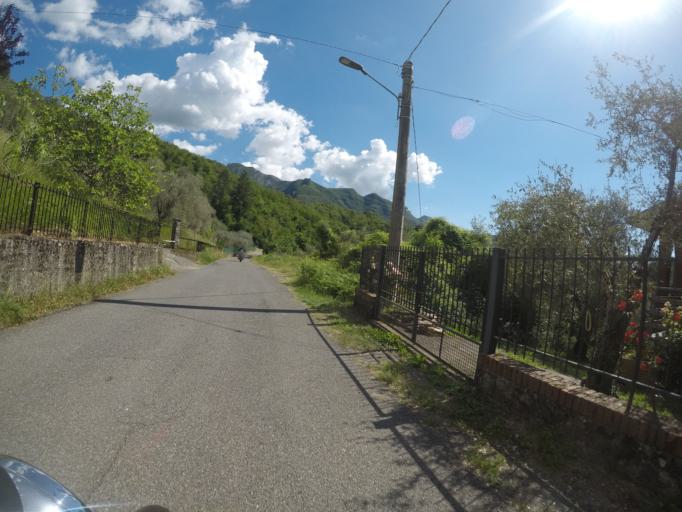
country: IT
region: Tuscany
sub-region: Provincia di Massa-Carrara
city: Casola in Lunigiana
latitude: 44.1785
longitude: 10.1521
